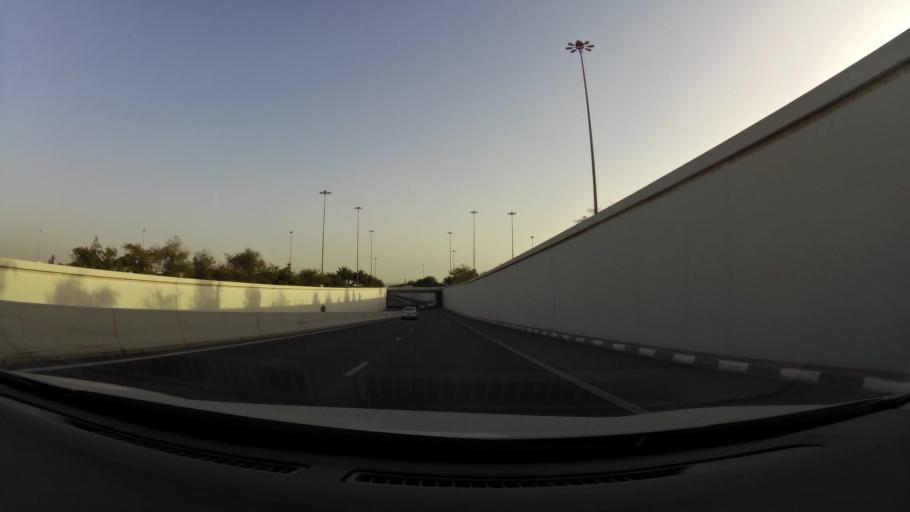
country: QA
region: Baladiyat ar Rayyan
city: Ar Rayyan
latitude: 25.3219
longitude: 51.4603
